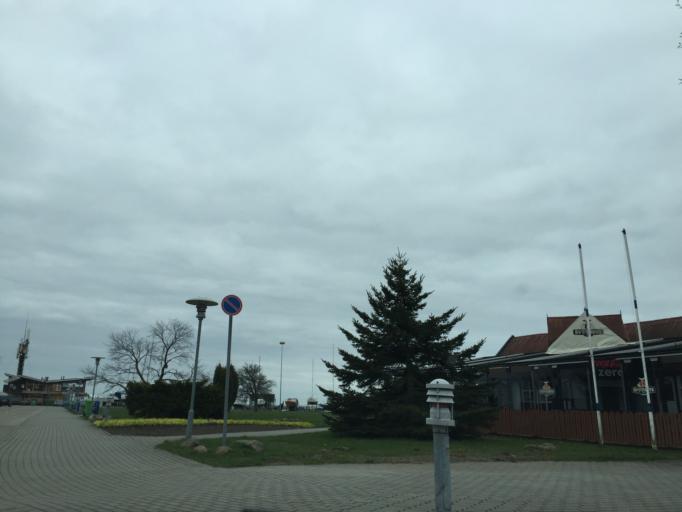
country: LT
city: Nida
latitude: 55.3032
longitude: 21.0067
